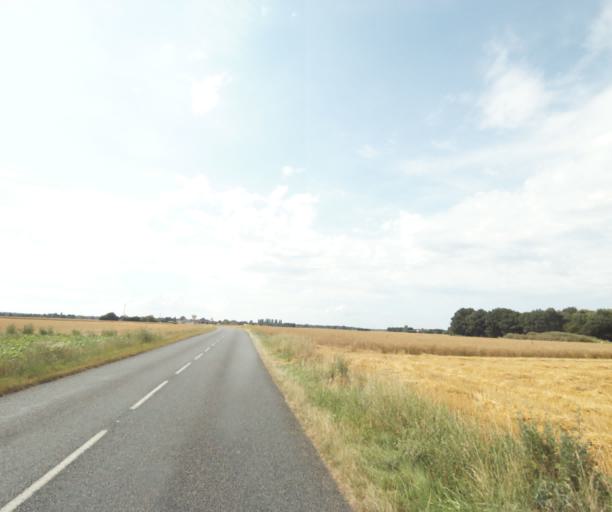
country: FR
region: Ile-de-France
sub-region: Departement de Seine-et-Marne
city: Acheres-la-Foret
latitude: 48.3481
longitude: 2.5844
